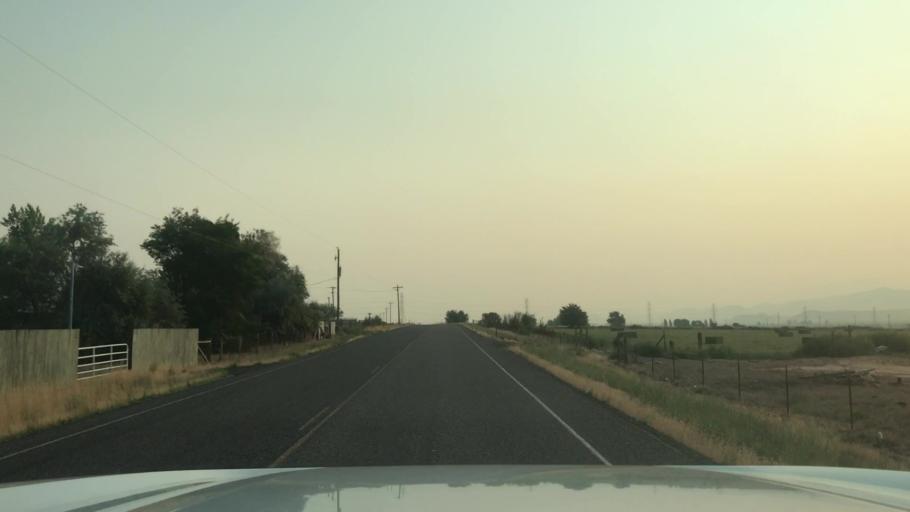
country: US
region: Utah
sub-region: Sevier County
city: Aurora
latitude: 38.8894
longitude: -111.9552
